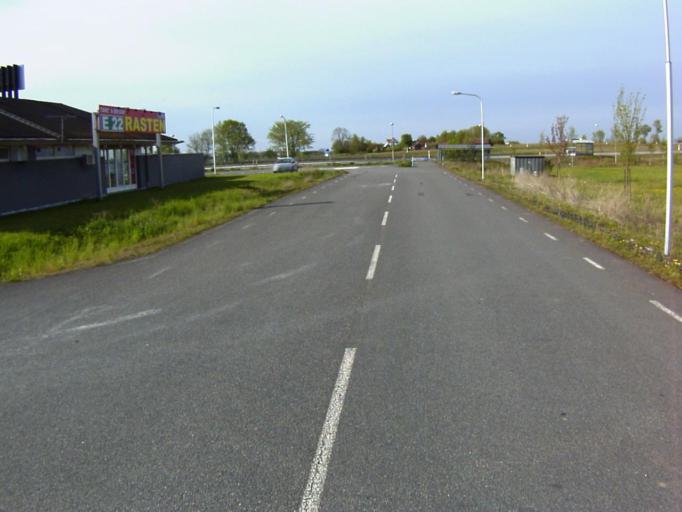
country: SE
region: Skane
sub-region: Kristianstads Kommun
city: Fjalkinge
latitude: 56.0353
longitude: 14.2685
